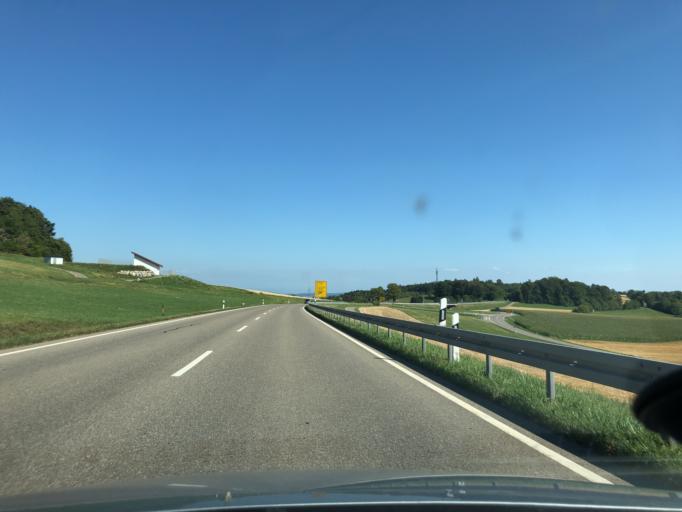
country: DE
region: Baden-Wuerttemberg
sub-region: Freiburg Region
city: Dogern
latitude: 47.6648
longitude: 8.1606
